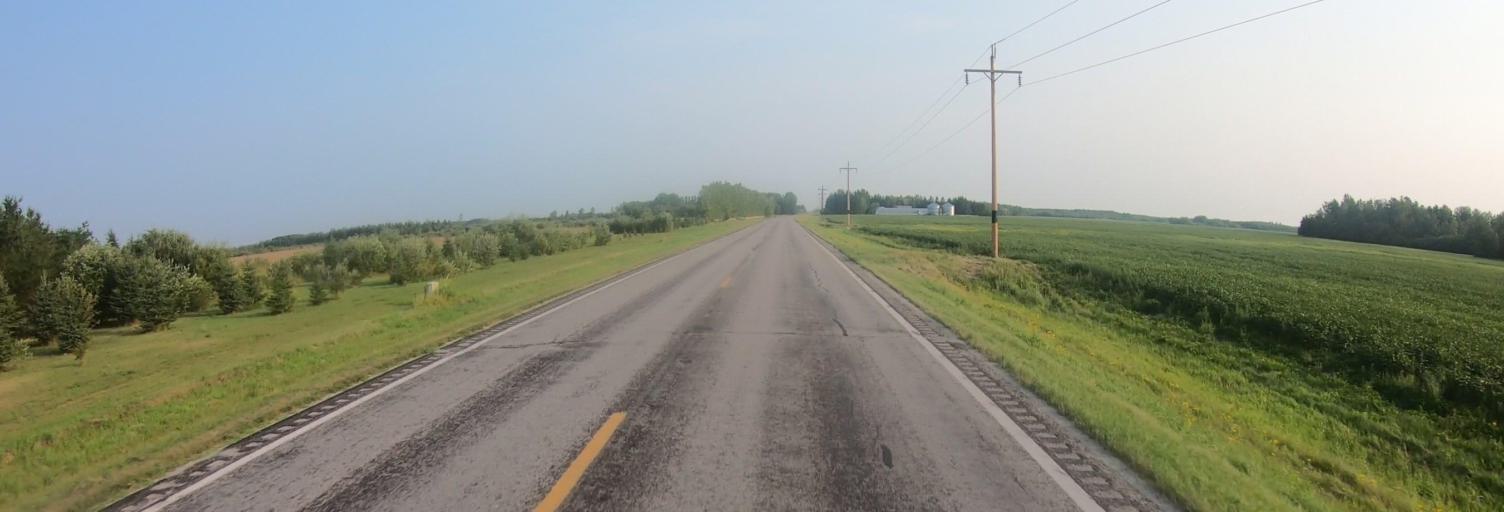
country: US
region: Minnesota
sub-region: Roseau County
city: Warroad
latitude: 48.7899
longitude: -95.3306
